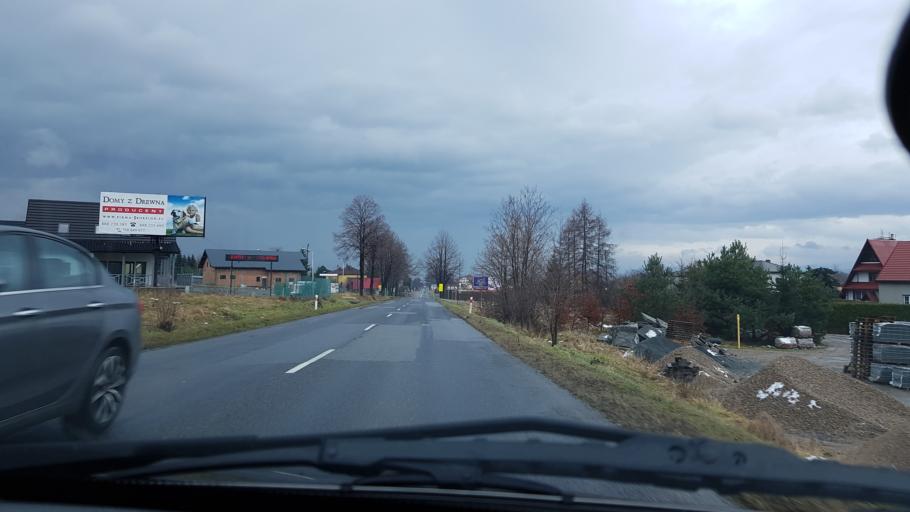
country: PL
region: Silesian Voivodeship
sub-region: Powiat bielski
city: Rybarzowice
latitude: 49.7332
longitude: 19.1177
